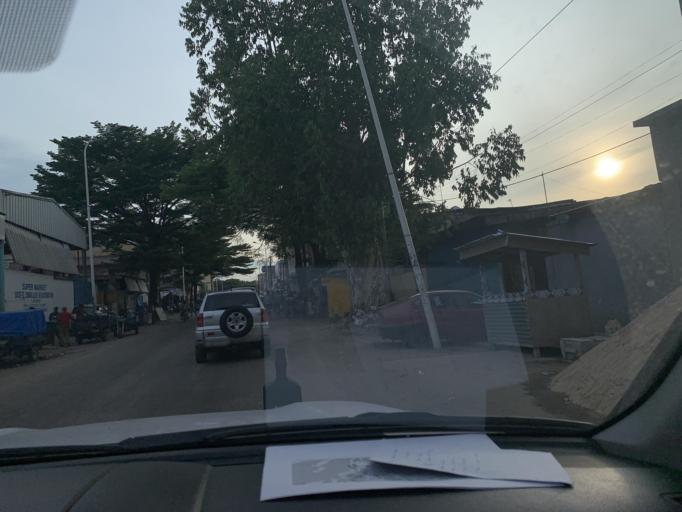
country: CG
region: Brazzaville
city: Brazzaville
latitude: -4.2642
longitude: 15.2878
